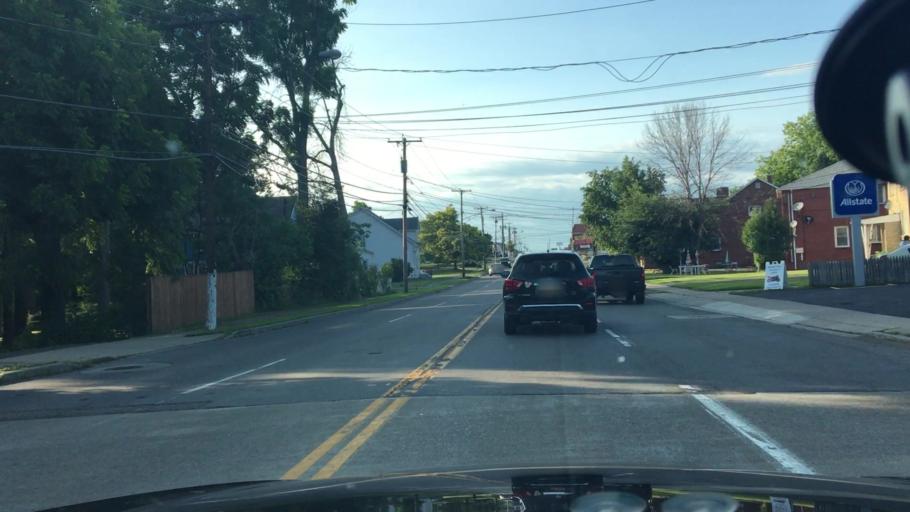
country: US
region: New York
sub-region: Erie County
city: Lackawanna
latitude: 42.8226
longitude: -78.8025
